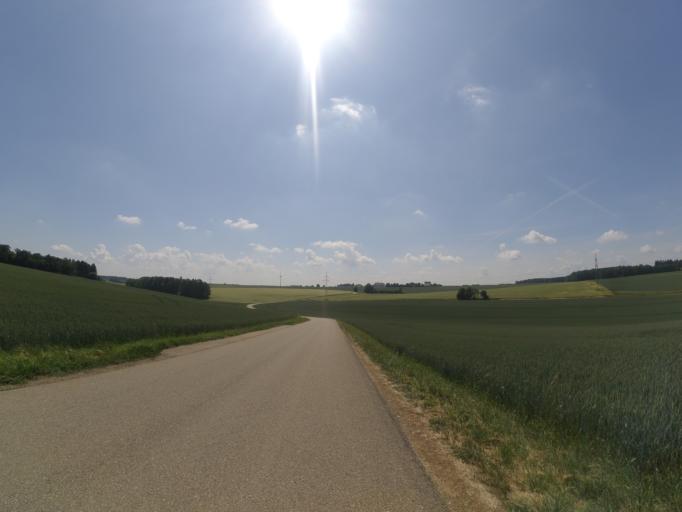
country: DE
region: Baden-Wuerttemberg
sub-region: Tuebingen Region
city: Bernstadt
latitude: 48.4664
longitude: 10.0217
